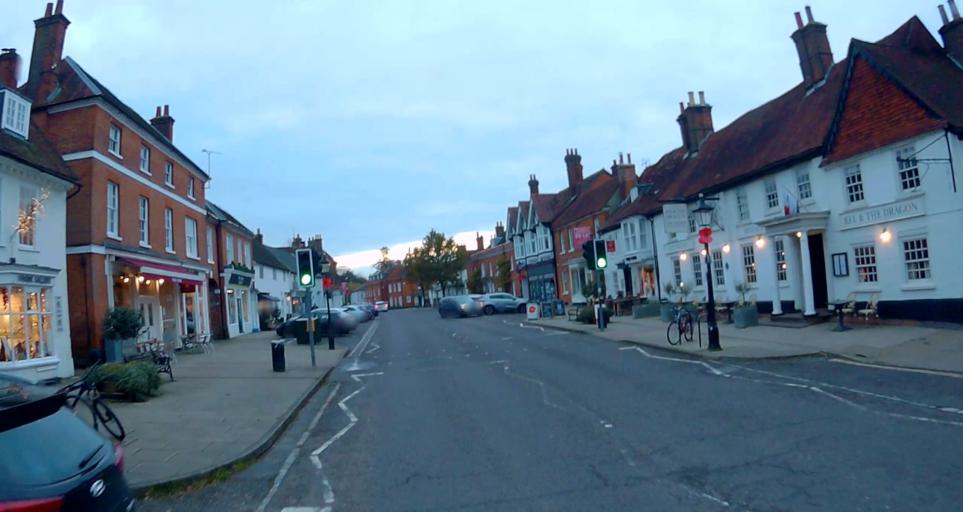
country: GB
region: England
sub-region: Hampshire
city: Odiham
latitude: 51.2541
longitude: -0.9396
